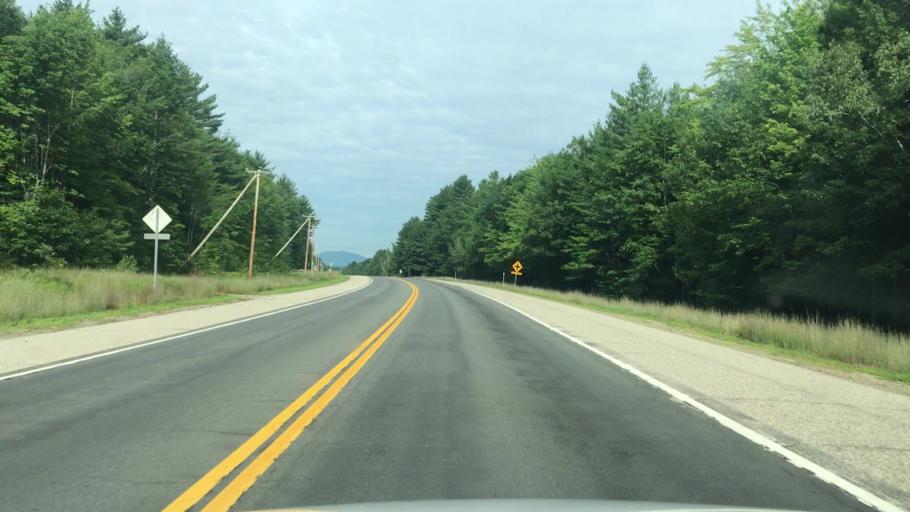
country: US
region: New Hampshire
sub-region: Carroll County
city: Tamworth
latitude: 43.8242
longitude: -71.2273
